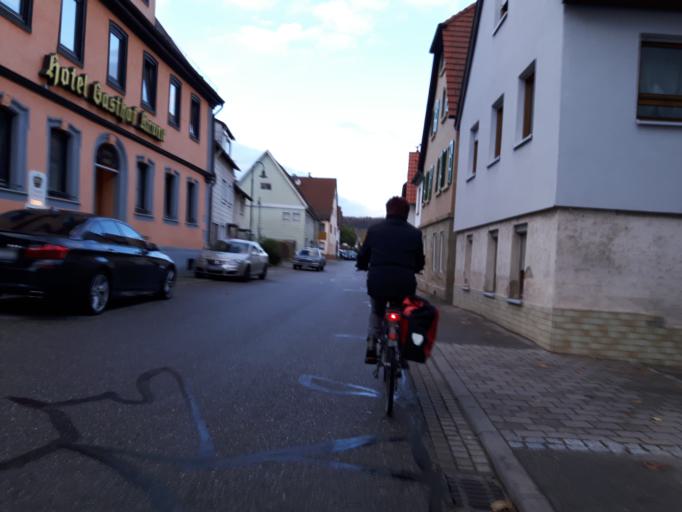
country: DE
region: Baden-Wuerttemberg
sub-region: Regierungsbezirk Stuttgart
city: Eberstadt
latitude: 49.1796
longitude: 9.3214
